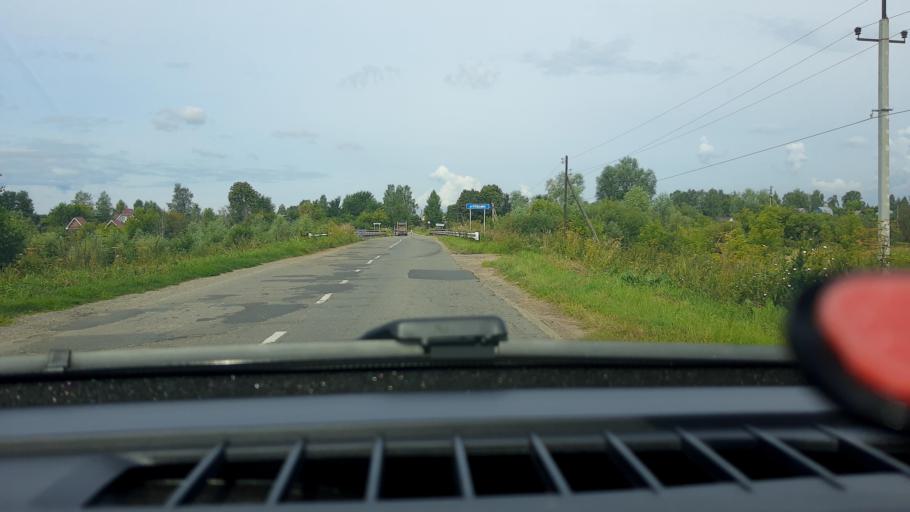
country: RU
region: Nizjnij Novgorod
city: Burevestnik
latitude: 56.0650
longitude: 43.6681
